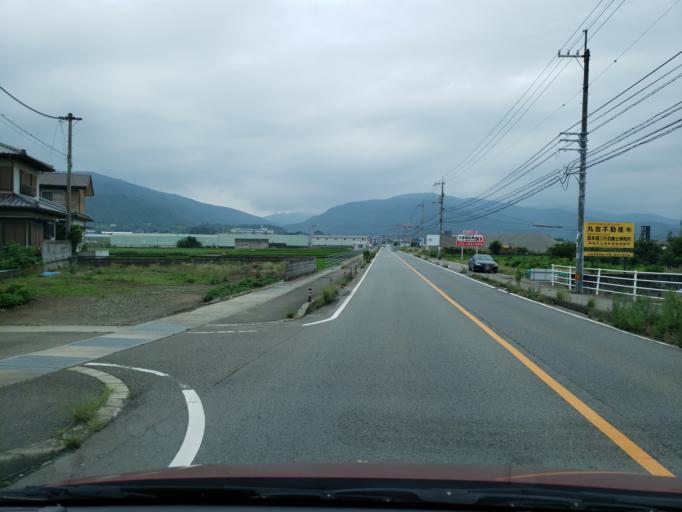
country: JP
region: Tokushima
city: Kamojimacho-jogejima
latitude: 34.1063
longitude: 134.3474
